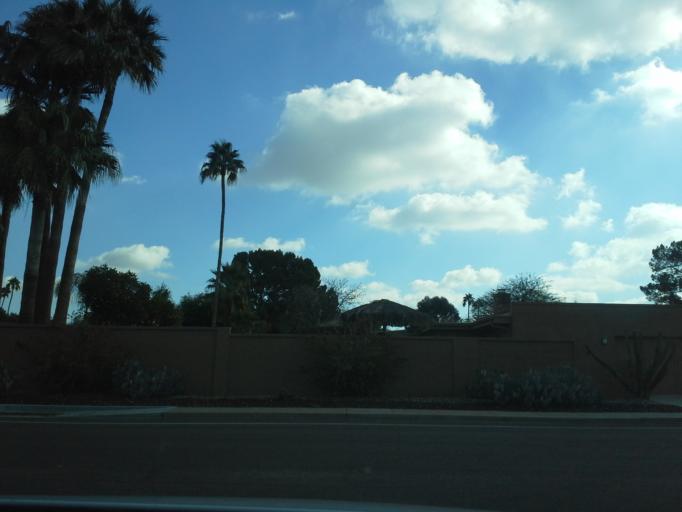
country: US
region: Arizona
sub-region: Maricopa County
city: Glendale
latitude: 33.6192
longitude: -112.0710
